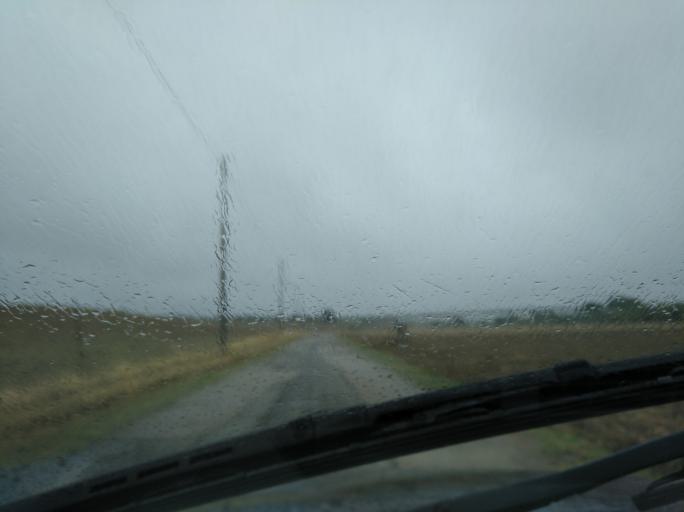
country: PT
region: Portalegre
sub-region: Campo Maior
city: Campo Maior
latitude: 38.9760
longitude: -7.0691
